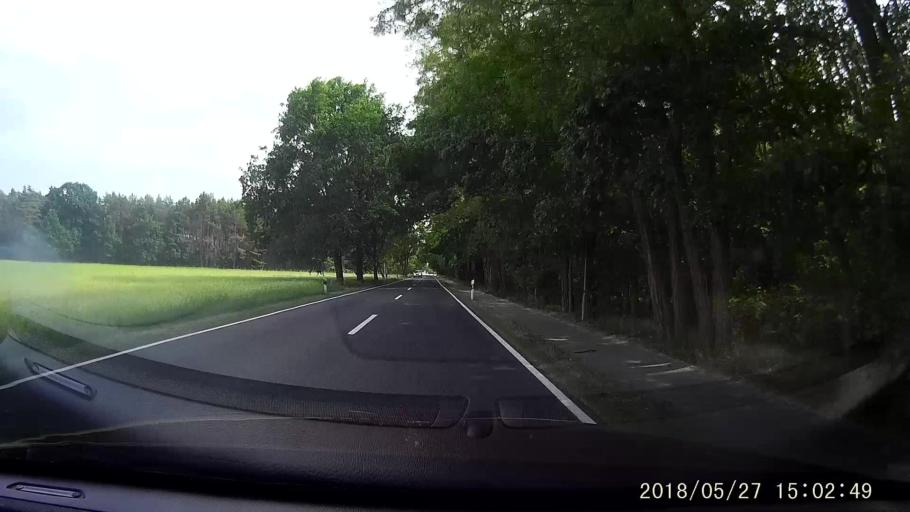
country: DE
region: Saxony
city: Mucka
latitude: 51.3247
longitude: 14.7027
